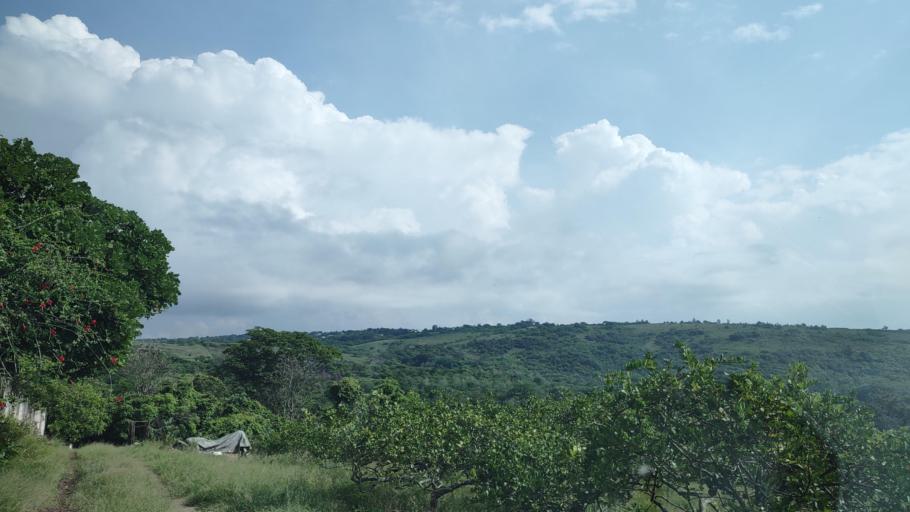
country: MX
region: Veracruz
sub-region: Emiliano Zapata
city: Dos Rios
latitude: 19.4526
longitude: -96.8283
